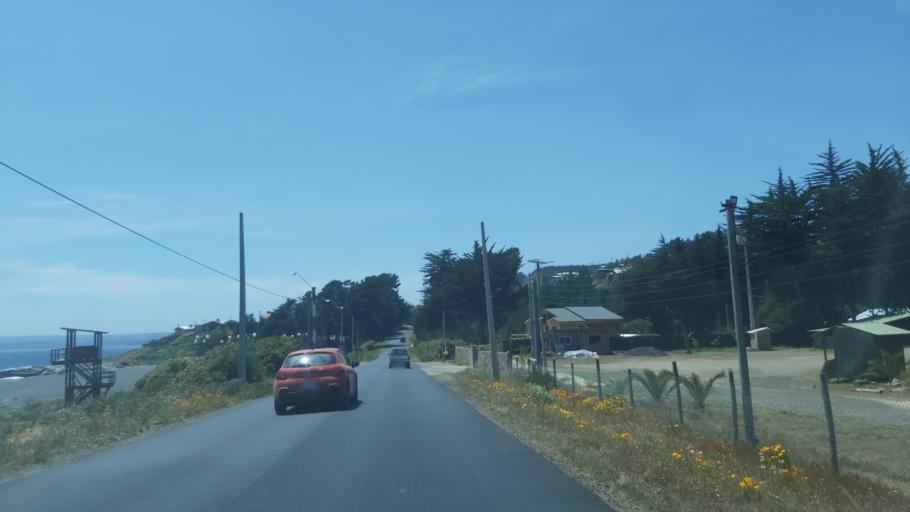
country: CL
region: Maule
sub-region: Provincia de Cauquenes
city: Cauquenes
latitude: -35.8265
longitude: -72.6117
